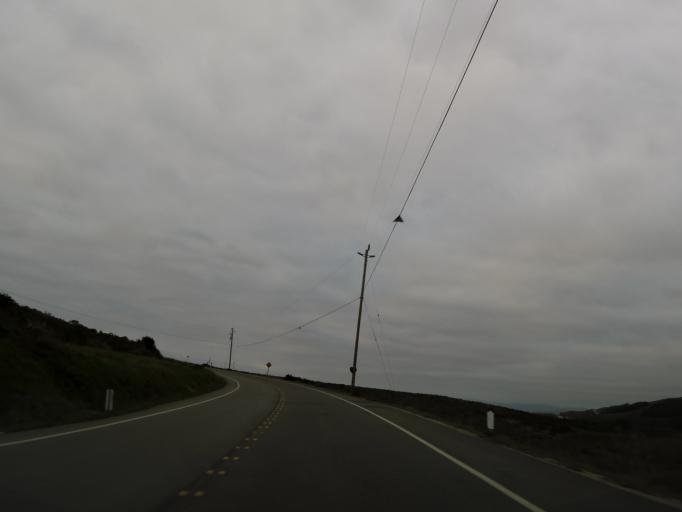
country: US
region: California
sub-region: San Mateo County
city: Half Moon Bay
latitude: 37.2581
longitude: -122.4091
